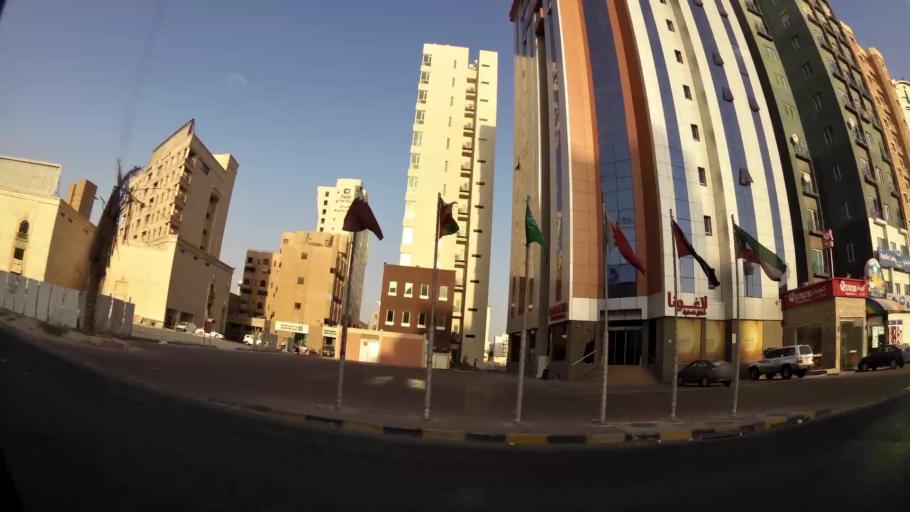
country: KW
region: Muhafazat Hawalli
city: As Salimiyah
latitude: 29.3391
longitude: 48.0700
